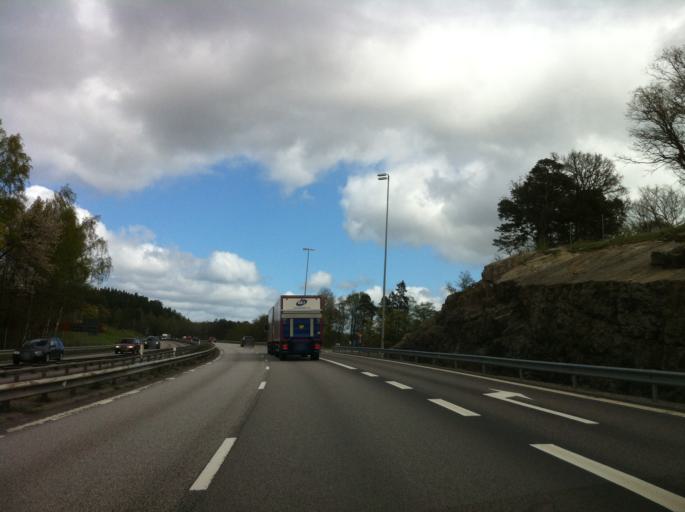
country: SE
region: Vaestra Goetaland
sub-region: Alingsas Kommun
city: Alingsas
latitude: 57.9037
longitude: 12.5003
